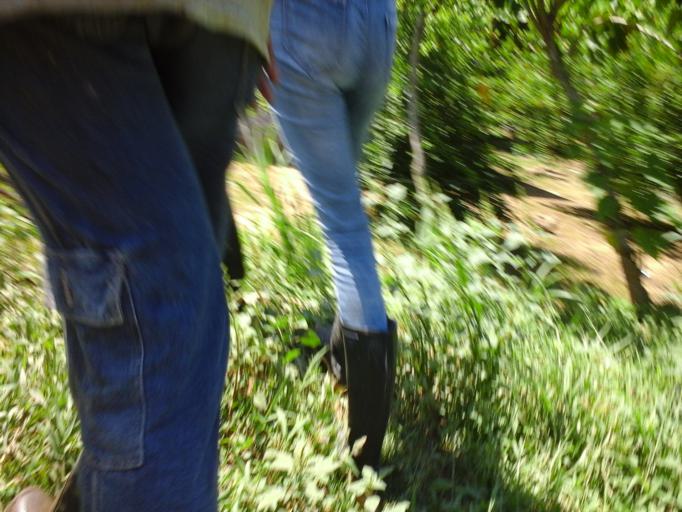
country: CO
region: Bolivar
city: San Pablo
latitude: 10.1613
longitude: -75.2747
